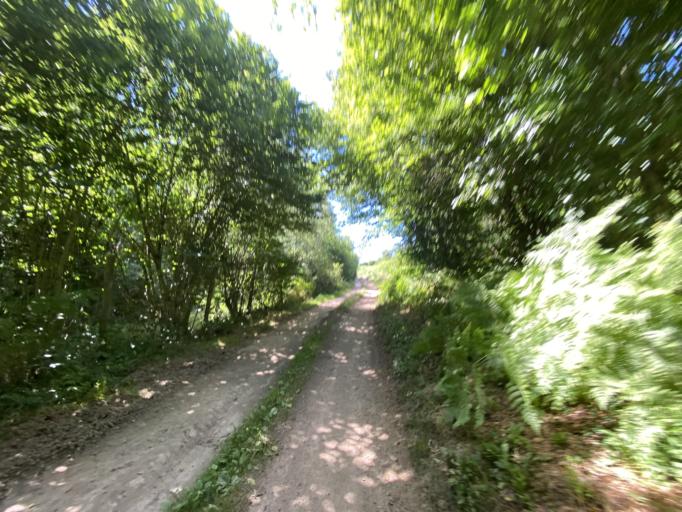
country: FR
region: Bourgogne
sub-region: Departement de la Cote-d'Or
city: Saulieu
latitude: 47.2885
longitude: 4.1286
